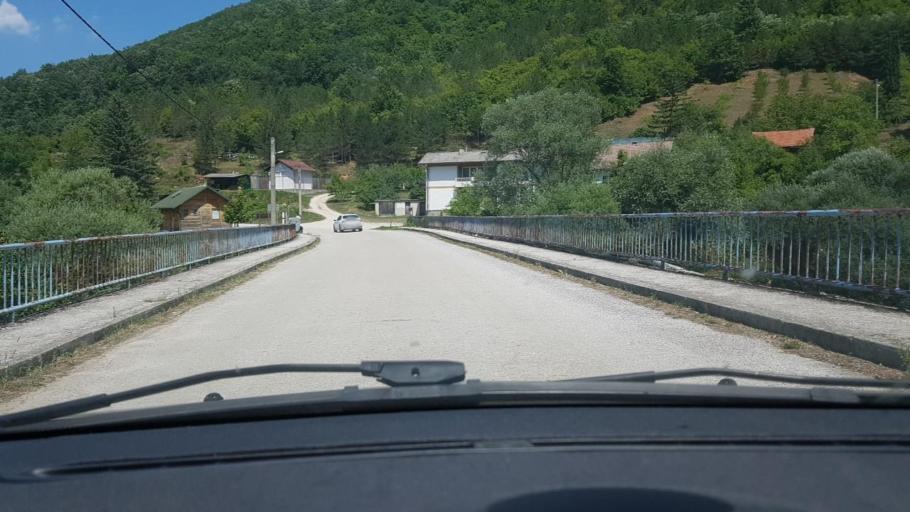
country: BA
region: Federation of Bosnia and Herzegovina
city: Orasac
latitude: 44.4929
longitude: 16.1430
